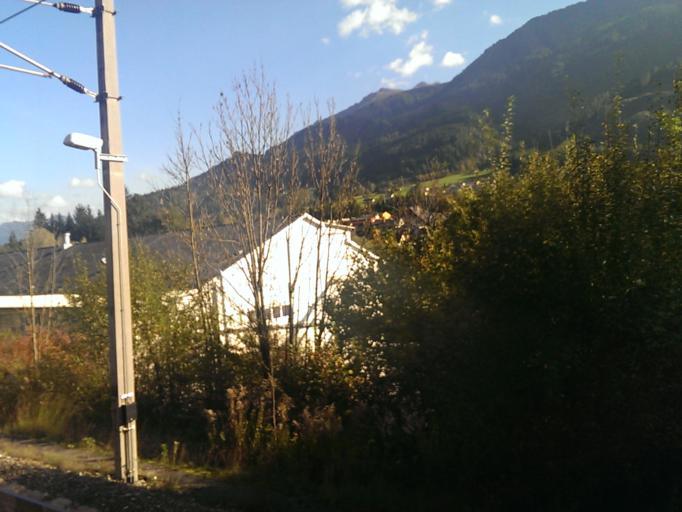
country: AT
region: Styria
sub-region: Politischer Bezirk Liezen
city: Rottenmann
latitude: 47.5278
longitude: 14.3586
